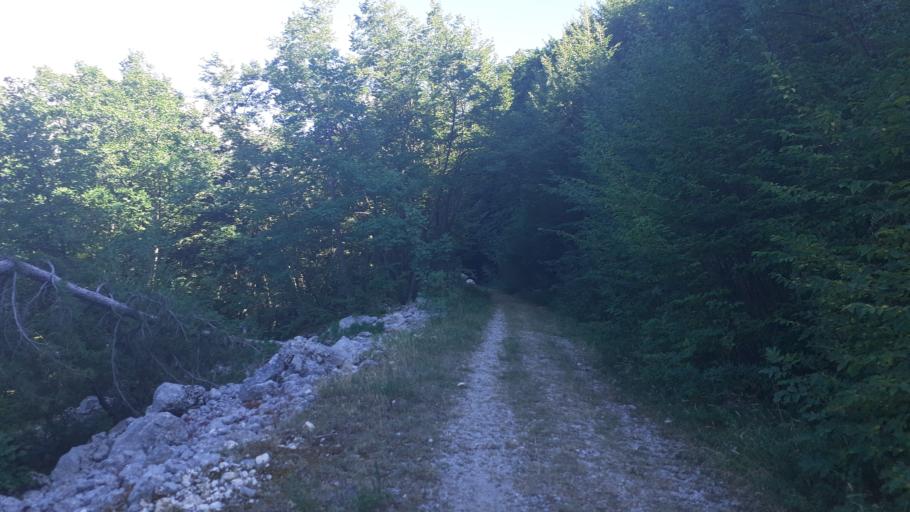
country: IT
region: Abruzzo
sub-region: Provincia di Pescara
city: Sant'Eufemia a Maiella
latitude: 42.1085
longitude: 14.0000
